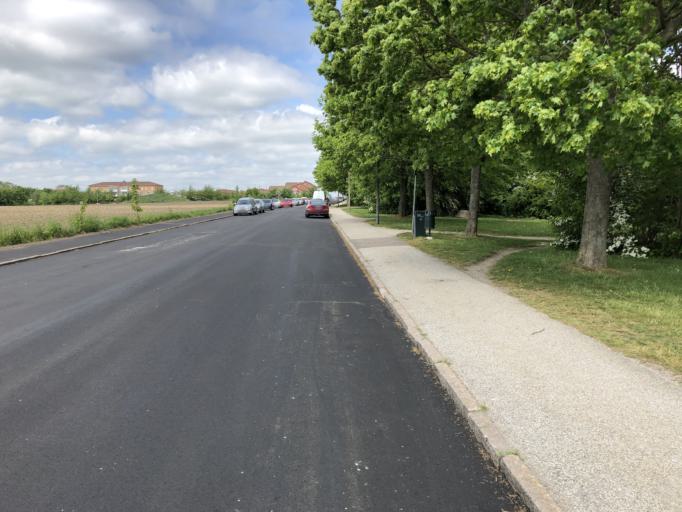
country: SE
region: Skane
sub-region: Lunds Kommun
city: Lund
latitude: 55.7010
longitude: 13.1616
